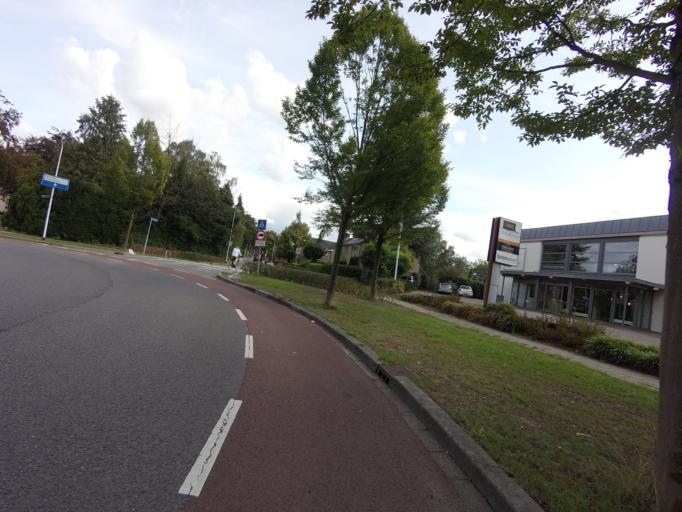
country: NL
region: Overijssel
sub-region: Gemeente Deventer
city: Schalkhaar
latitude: 52.2670
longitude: 6.1847
